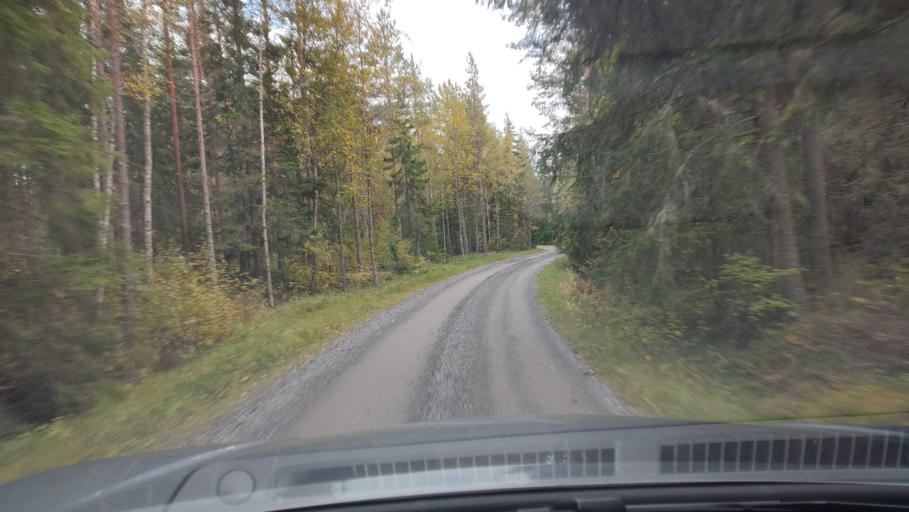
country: FI
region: Ostrobothnia
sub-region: Sydosterbotten
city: Kristinestad
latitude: 62.2338
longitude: 21.4012
